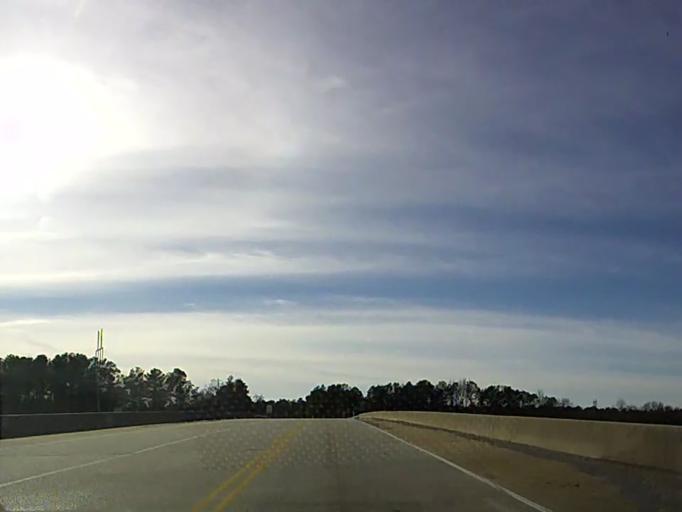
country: US
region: Georgia
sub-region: Monroe County
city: Forsyth
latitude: 32.9914
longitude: -83.8444
